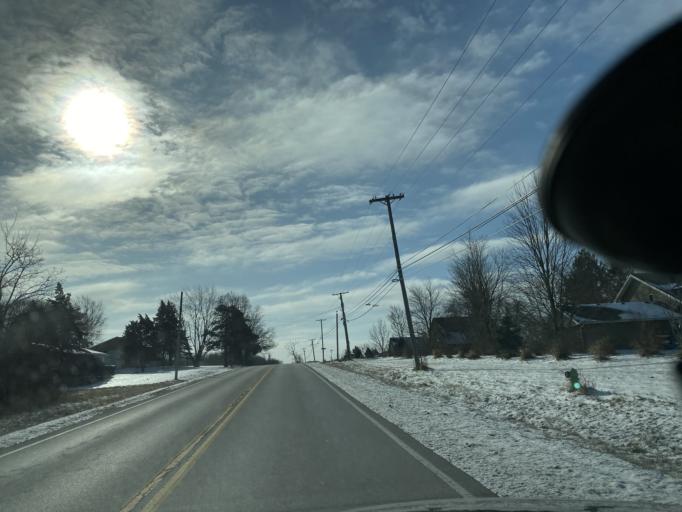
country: US
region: Illinois
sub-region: Will County
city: Goodings Grove
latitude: 41.6634
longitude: -87.9320
